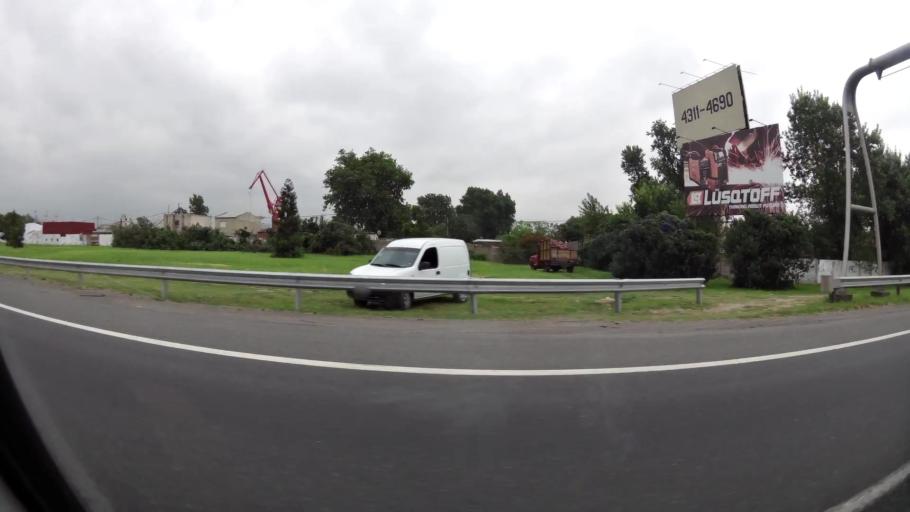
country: AR
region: Buenos Aires
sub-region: Partido de Avellaneda
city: Avellaneda
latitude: -34.6477
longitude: -58.3517
